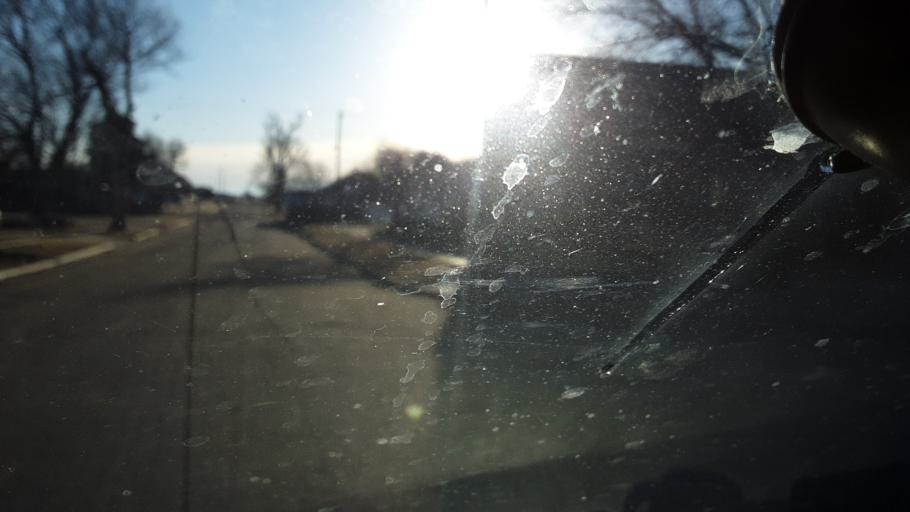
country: US
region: Kansas
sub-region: Rice County
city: Lyons
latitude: 38.3543
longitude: -98.3482
